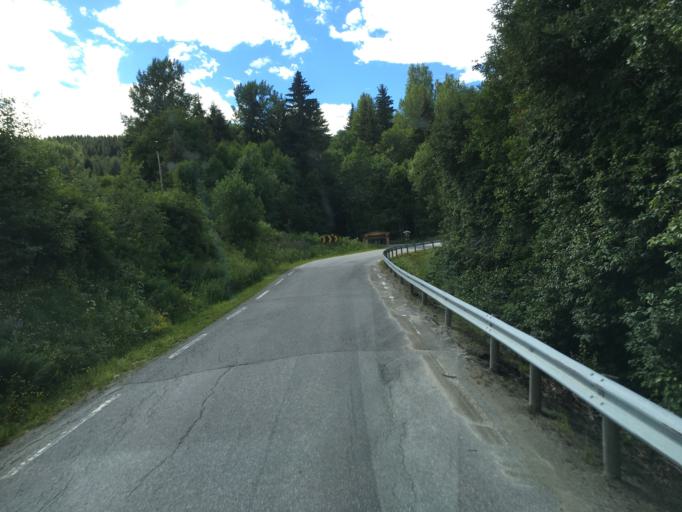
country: NO
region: Oppland
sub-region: Sondre Land
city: Hov
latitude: 60.6960
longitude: 10.2887
